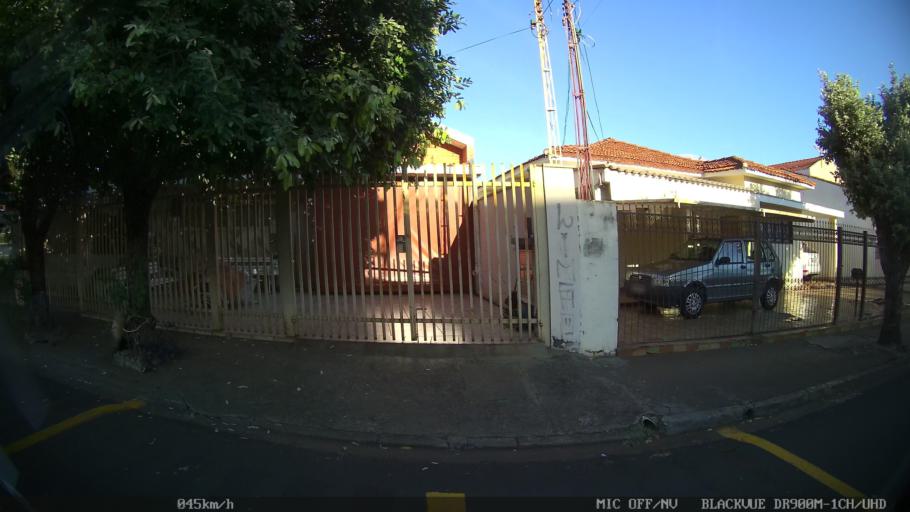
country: BR
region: Sao Paulo
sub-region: Sao Jose Do Rio Preto
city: Sao Jose do Rio Preto
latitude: -20.8020
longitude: -49.3682
